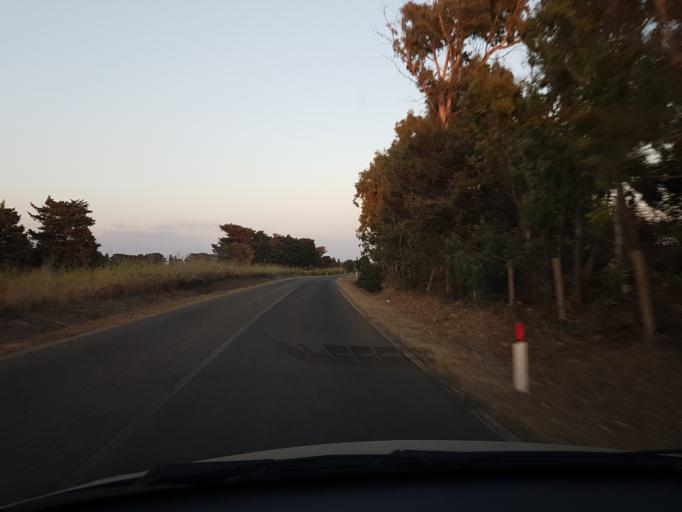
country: IT
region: Sardinia
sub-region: Provincia di Oristano
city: Riola Sardo
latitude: 39.9983
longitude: 8.4891
